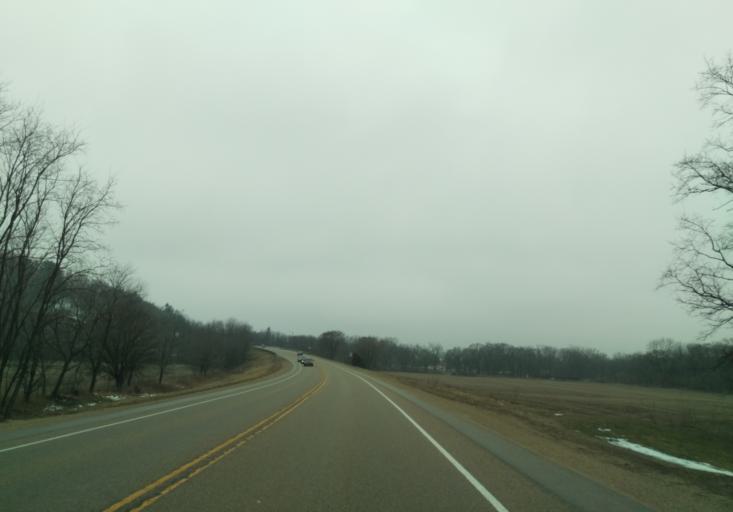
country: US
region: Wisconsin
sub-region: Dane County
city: Mazomanie
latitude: 43.1721
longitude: -89.7836
